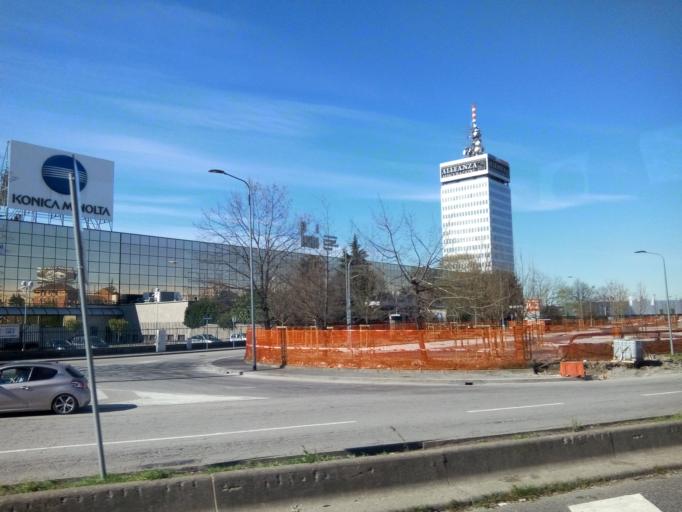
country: IT
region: Lombardy
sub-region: Citta metropolitana di Milano
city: Baranzate
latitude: 45.5107
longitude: 9.1284
